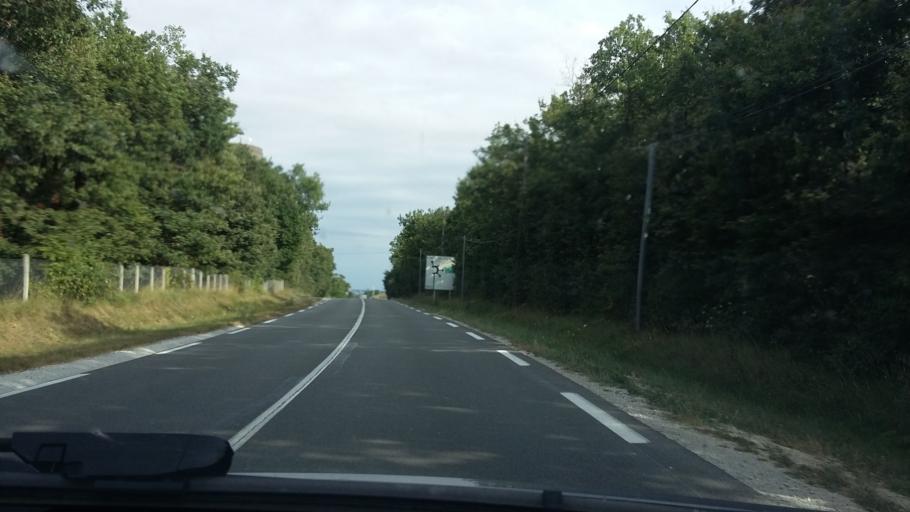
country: FR
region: Poitou-Charentes
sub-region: Departement de la Charente
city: Balzac
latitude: 45.6947
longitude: 0.0997
